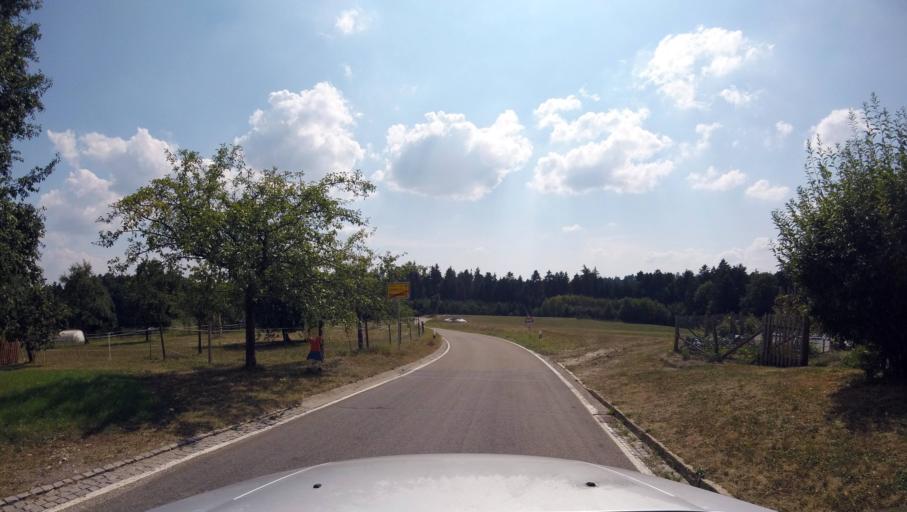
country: DE
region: Baden-Wuerttemberg
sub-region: Regierungsbezirk Stuttgart
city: Alfdorf
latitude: 48.8712
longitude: 9.7014
